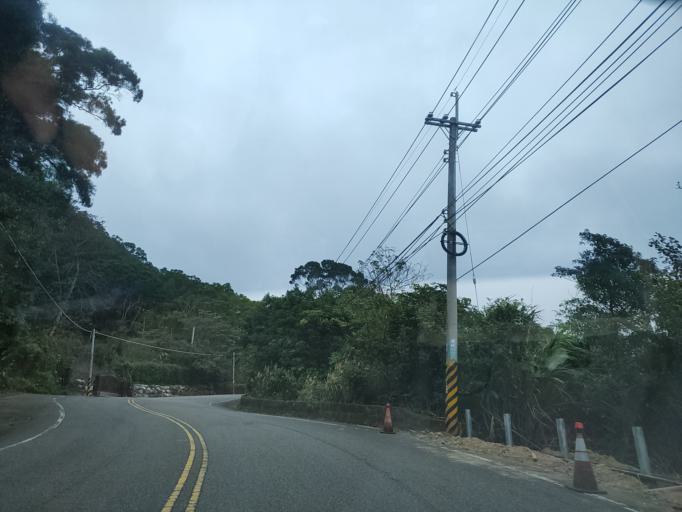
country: TW
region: Taiwan
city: Fengyuan
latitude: 24.3701
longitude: 120.7740
